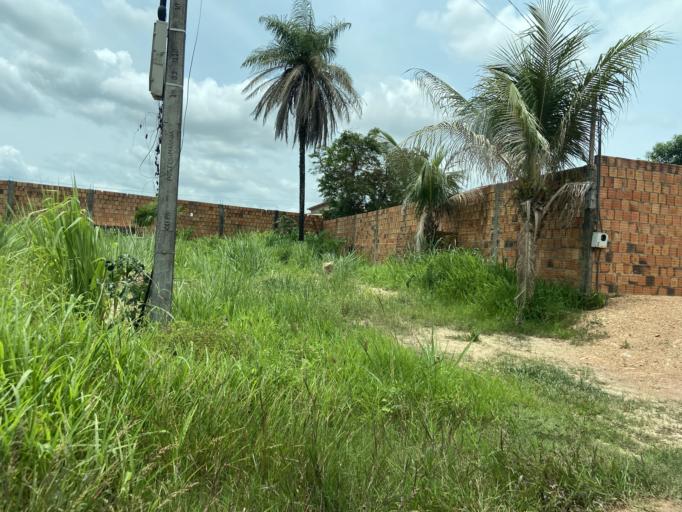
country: BR
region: Para
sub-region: Maraba
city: Maraba
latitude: -5.3554
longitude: -49.0727
